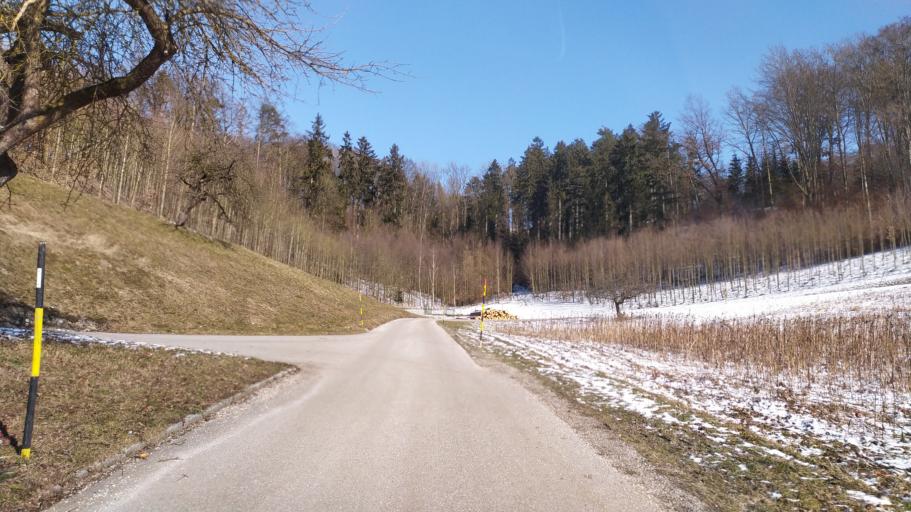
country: AT
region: Upper Austria
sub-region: Politischer Bezirk Urfahr-Umgebung
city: Ottensheim
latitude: 48.3325
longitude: 14.2032
